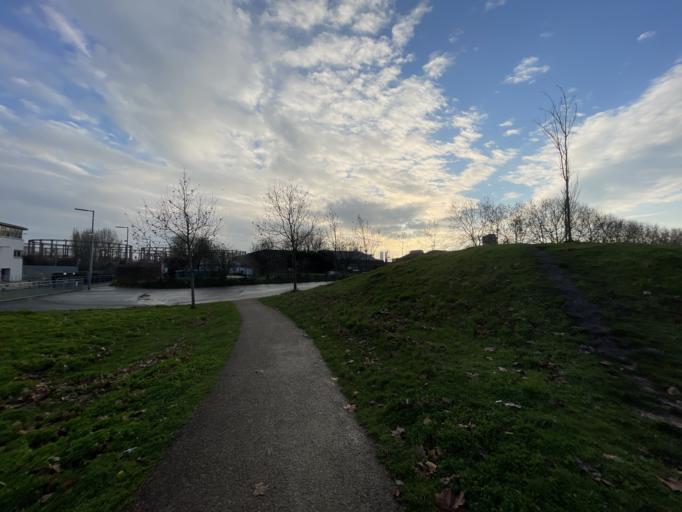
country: GB
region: England
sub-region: Greater London
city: Poplar
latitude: 51.5285
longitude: -0.0047
